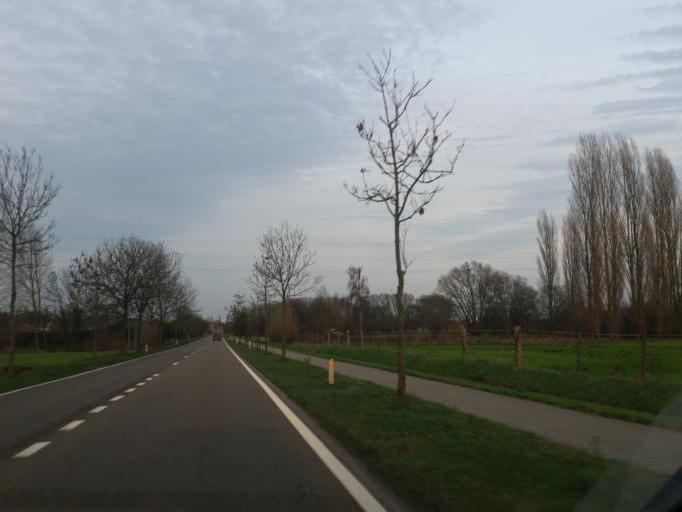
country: BE
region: Flanders
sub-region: Provincie Antwerpen
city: Duffel
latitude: 51.0948
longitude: 4.5212
